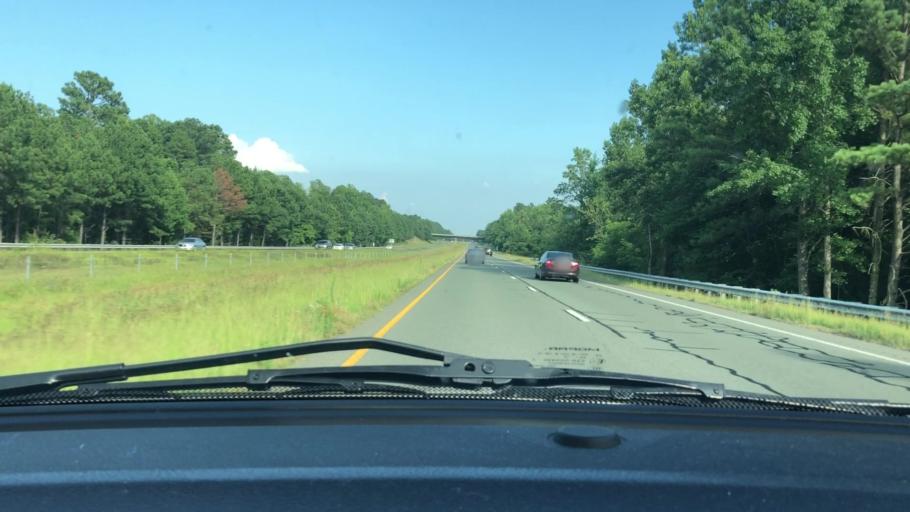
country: US
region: North Carolina
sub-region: Chatham County
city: Siler City
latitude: 35.7561
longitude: -79.4603
